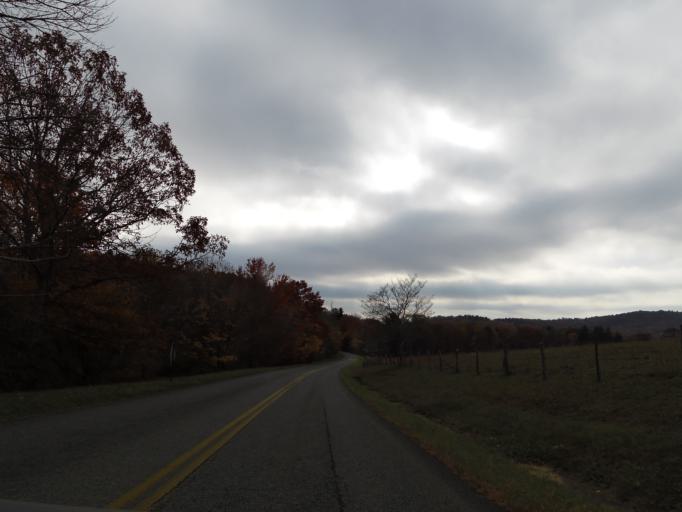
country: US
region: Virginia
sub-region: Carroll County
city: Cana
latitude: 36.6593
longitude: -80.7002
